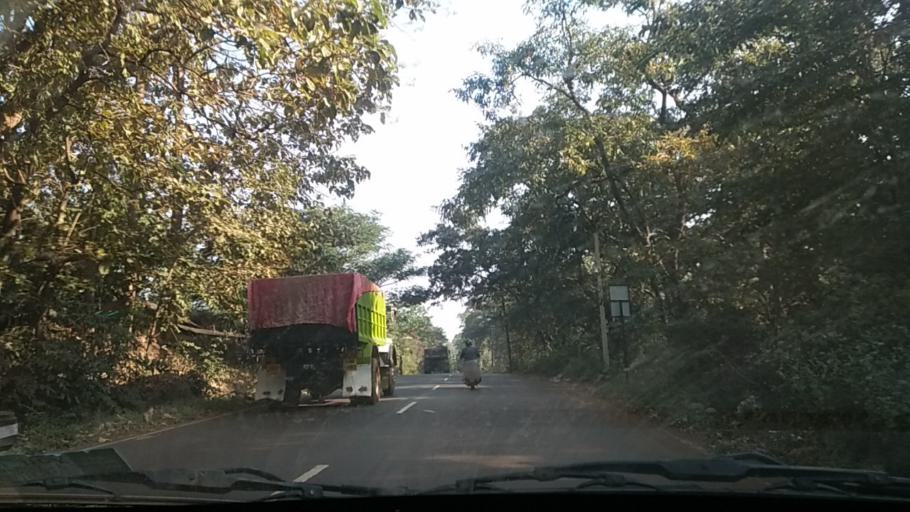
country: IN
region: Goa
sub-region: South Goa
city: Sanvordem
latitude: 15.2838
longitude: 74.1278
